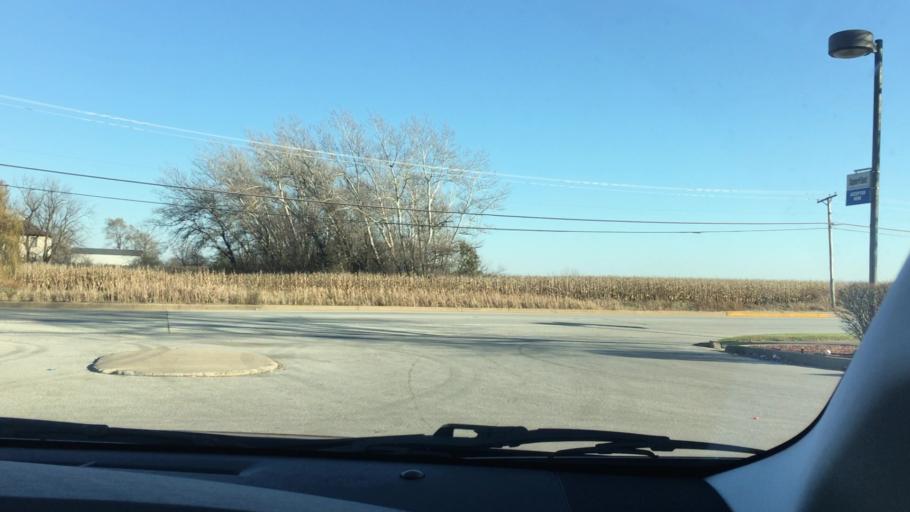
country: US
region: Illinois
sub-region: Will County
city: Frankfort Square
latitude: 41.5309
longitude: -87.7908
